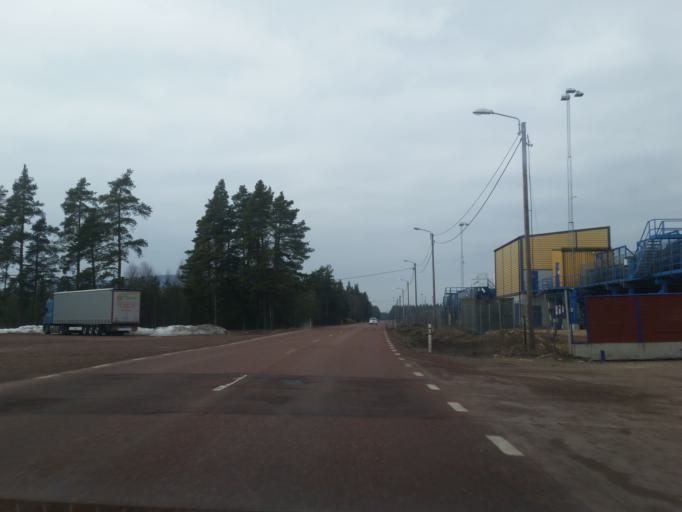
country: SE
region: Dalarna
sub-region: Alvdalens Kommun
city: AElvdalen
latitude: 61.1508
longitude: 14.1399
